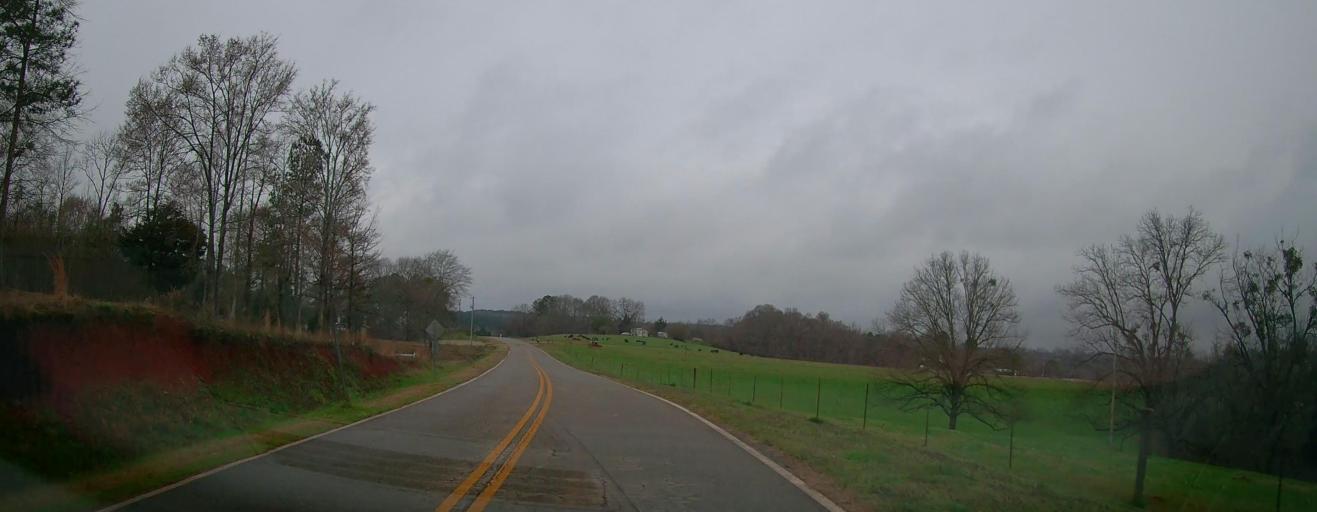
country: US
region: Georgia
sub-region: Monroe County
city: Forsyth
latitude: 33.0459
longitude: -83.8740
